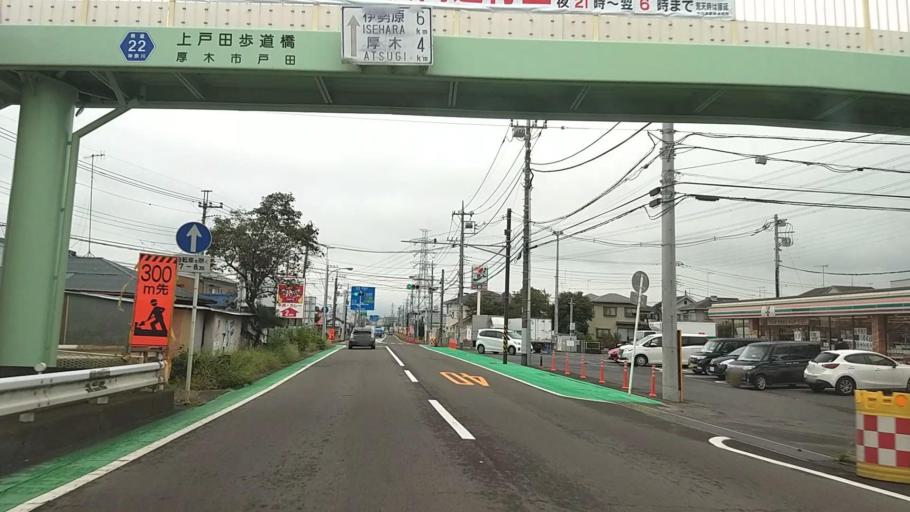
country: JP
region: Kanagawa
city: Atsugi
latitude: 35.4051
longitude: 139.3651
